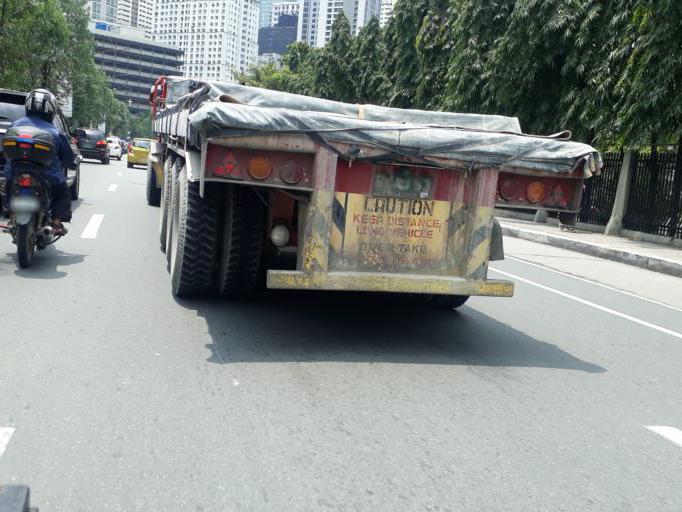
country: PH
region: Metro Manila
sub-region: Pasig
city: Pasig City
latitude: 14.5889
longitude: 121.0665
